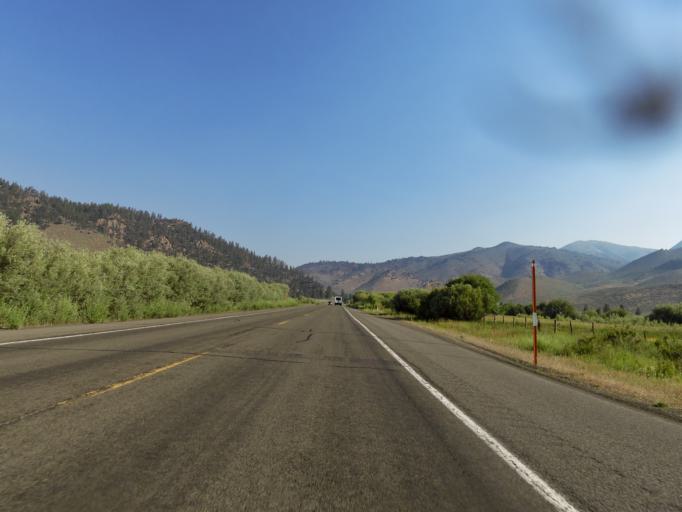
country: US
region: California
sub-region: Mono County
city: Bridgeport
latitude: 38.3300
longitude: -119.3176
